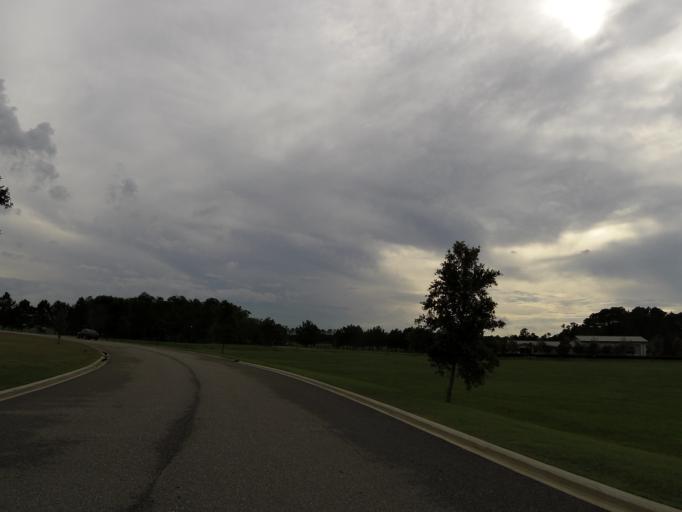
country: US
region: Florida
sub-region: Nassau County
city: Nassau Village-Ratliff
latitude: 30.5477
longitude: -81.7216
